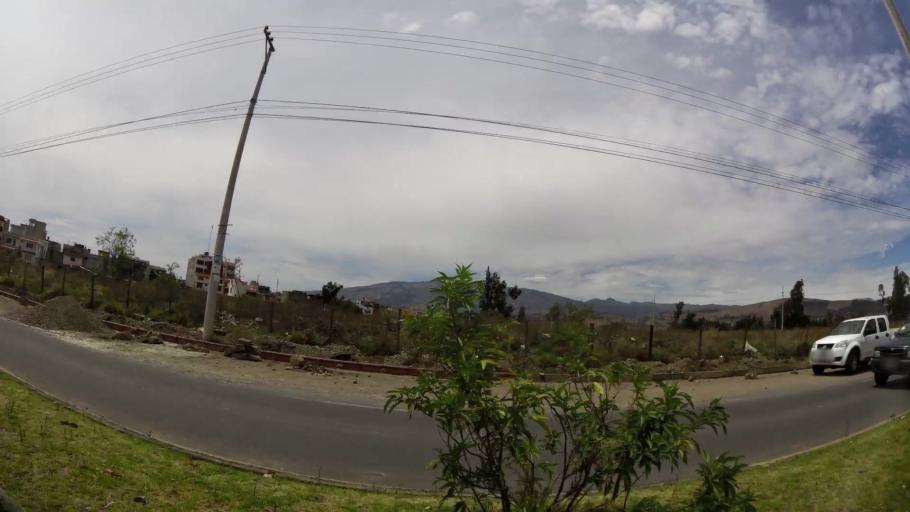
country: EC
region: Cotopaxi
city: San Miguel de Salcedo
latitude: -1.0395
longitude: -78.5860
